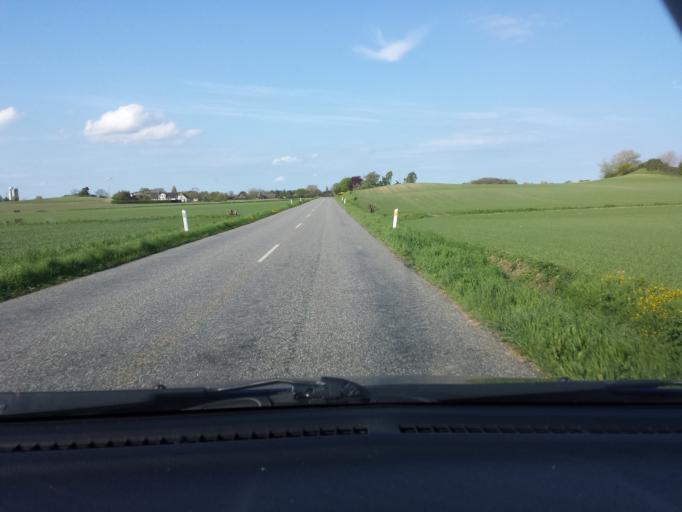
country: DK
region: South Denmark
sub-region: Langeland Kommune
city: Rudkobing
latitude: 54.8706
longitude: 10.7392
